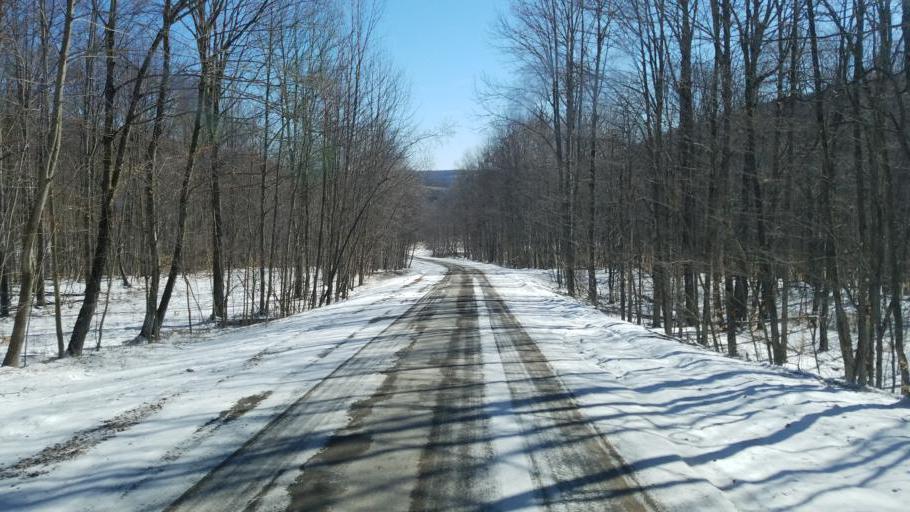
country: US
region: New York
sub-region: Allegany County
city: Wellsville
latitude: 42.0507
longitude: -77.9974
